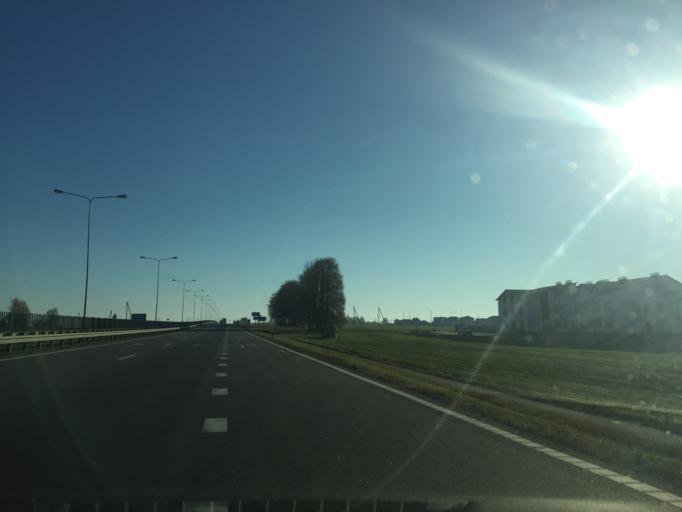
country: BY
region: Minsk
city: Smilavichy
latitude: 53.7595
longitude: 27.9911
